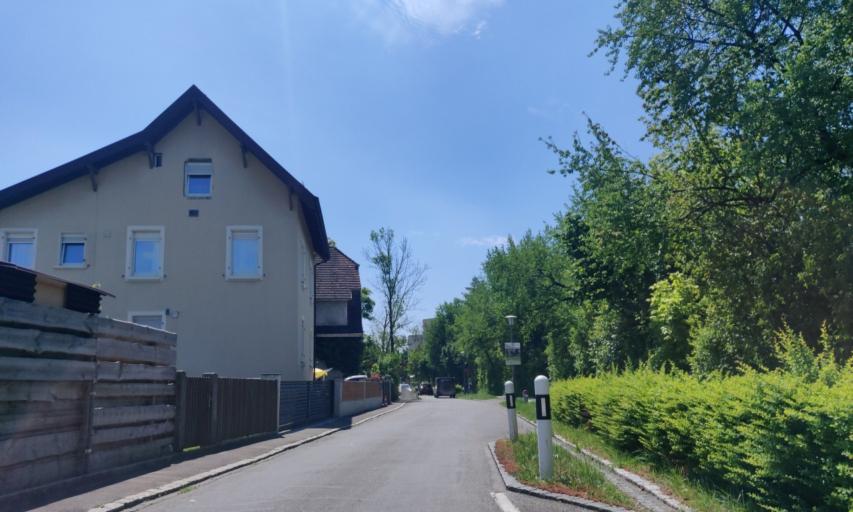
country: CH
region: Basel-Landschaft
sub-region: Bezirk Arlesheim
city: Munchenstein
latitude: 47.5250
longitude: 7.6183
